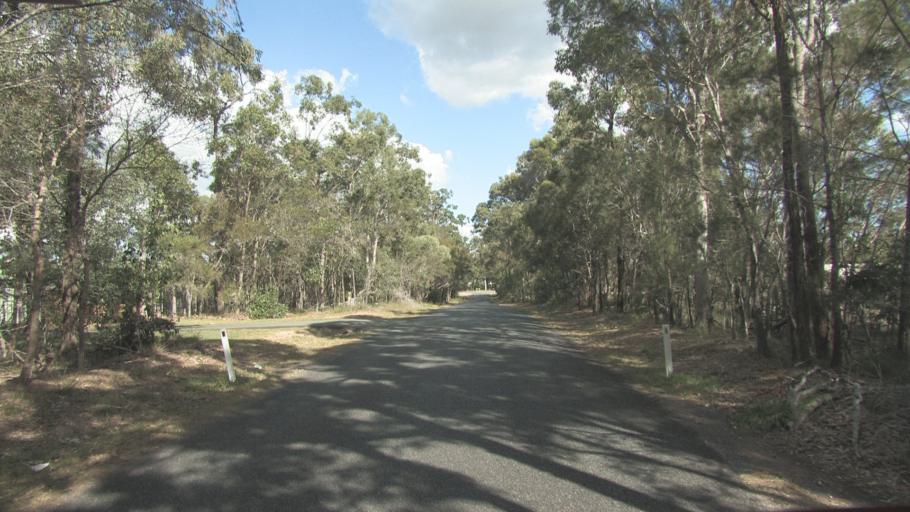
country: AU
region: Queensland
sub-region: Logan
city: Beenleigh
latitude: -27.6553
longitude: 153.2296
